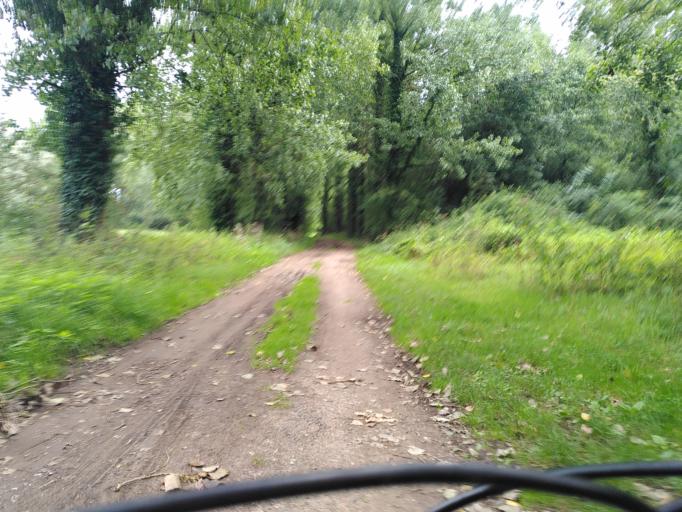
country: FR
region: Nord-Pas-de-Calais
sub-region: Departement du Pas-de-Calais
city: Mametz
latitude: 50.6391
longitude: 2.3050
